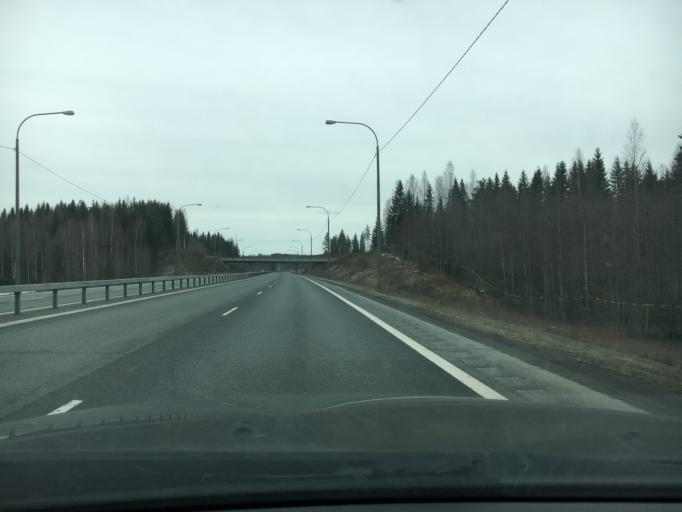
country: FI
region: Northern Savo
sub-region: Kuopio
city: Kuopio
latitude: 62.7428
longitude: 27.5856
